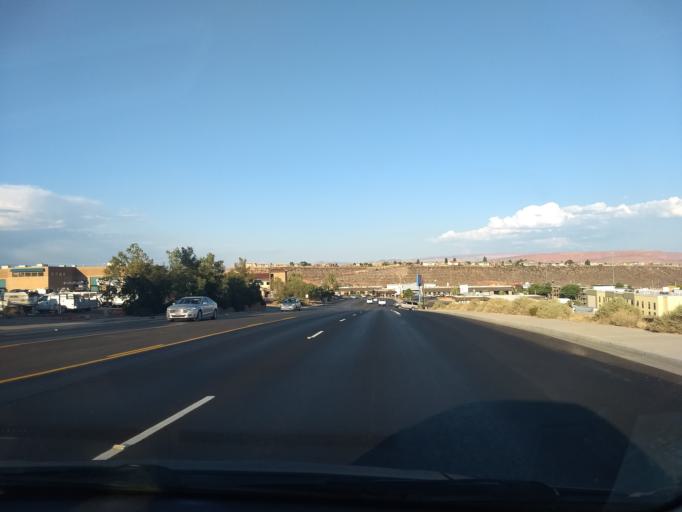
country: US
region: Utah
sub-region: Washington County
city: Saint George
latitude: 37.1122
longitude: -113.5655
